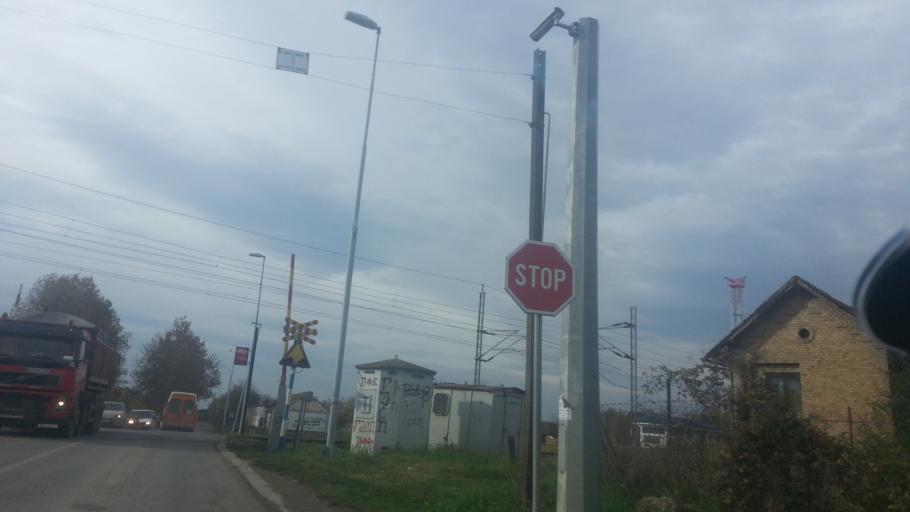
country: RS
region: Autonomna Pokrajina Vojvodina
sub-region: Sremski Okrug
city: Stara Pazova
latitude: 44.9834
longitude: 20.1401
